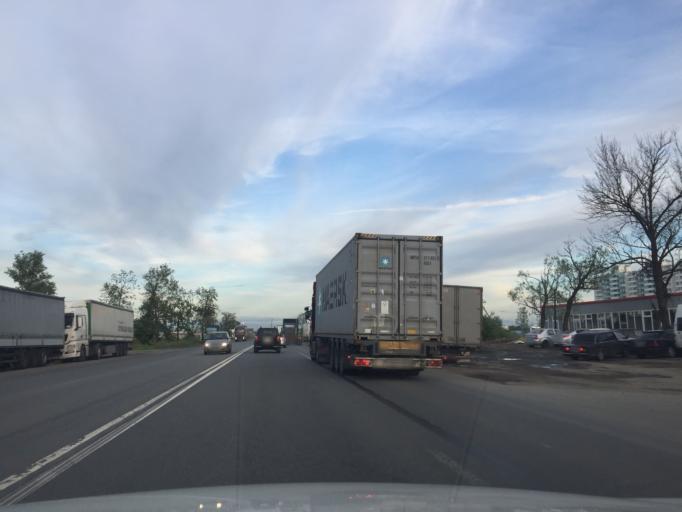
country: RU
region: St.-Petersburg
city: Petro-Slavyanka
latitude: 59.7591
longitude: 30.4771
